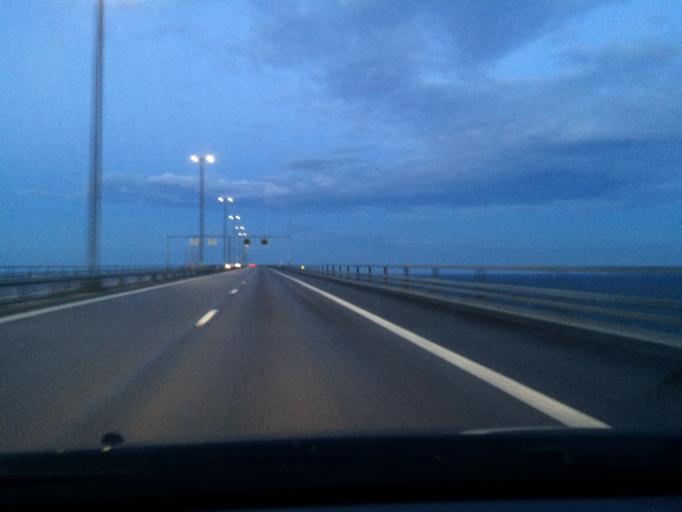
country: DK
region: Capital Region
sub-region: Dragor Kommune
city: Dragor
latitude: 55.5883
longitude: 12.7786
